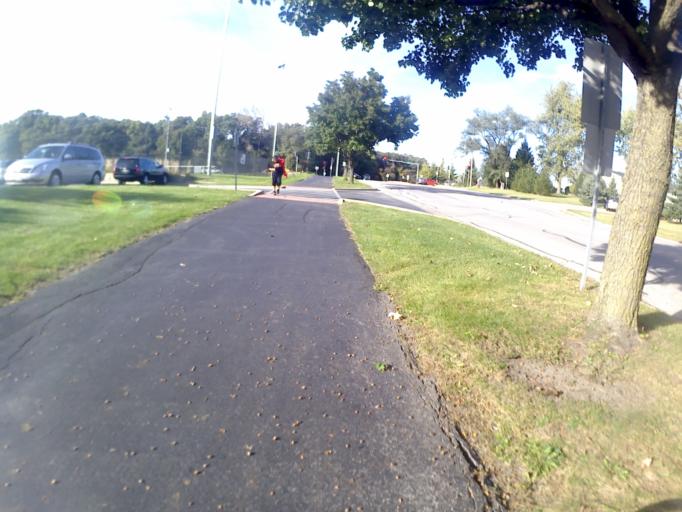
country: US
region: Illinois
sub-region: DuPage County
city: Woodridge
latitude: 41.7492
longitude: -88.0523
